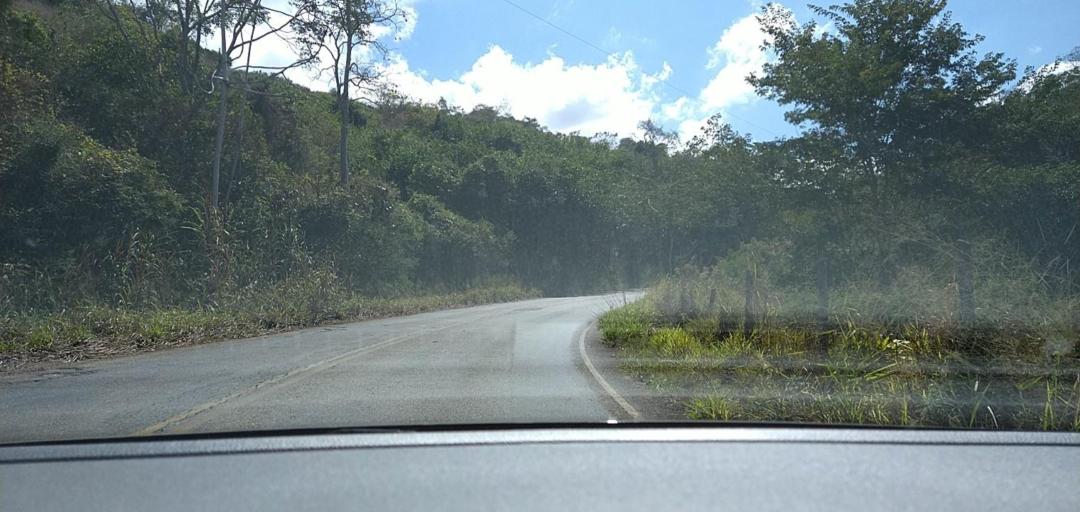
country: BR
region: Minas Gerais
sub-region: Ponte Nova
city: Ponte Nova
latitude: -20.2739
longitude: -42.9029
